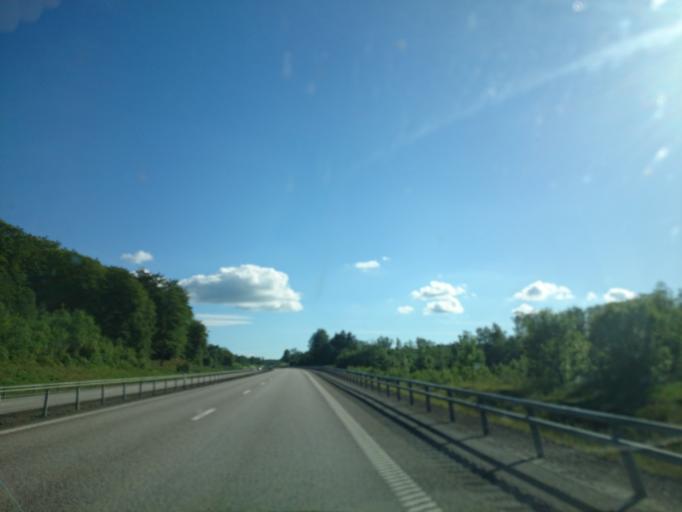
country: SE
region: Skane
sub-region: Orkelljunga Kommun
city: OErkelljunga
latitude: 56.3071
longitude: 13.3998
